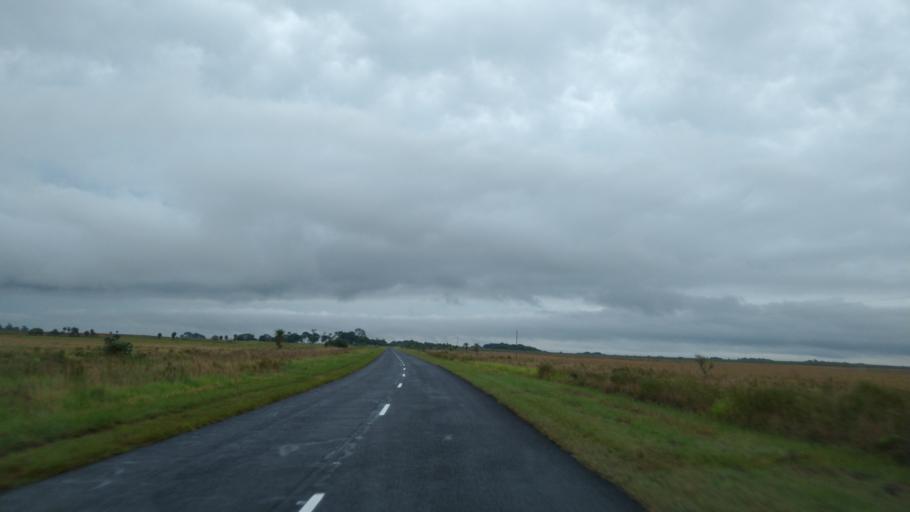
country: AR
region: Corrientes
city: Loreto
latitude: -27.7182
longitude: -57.2300
